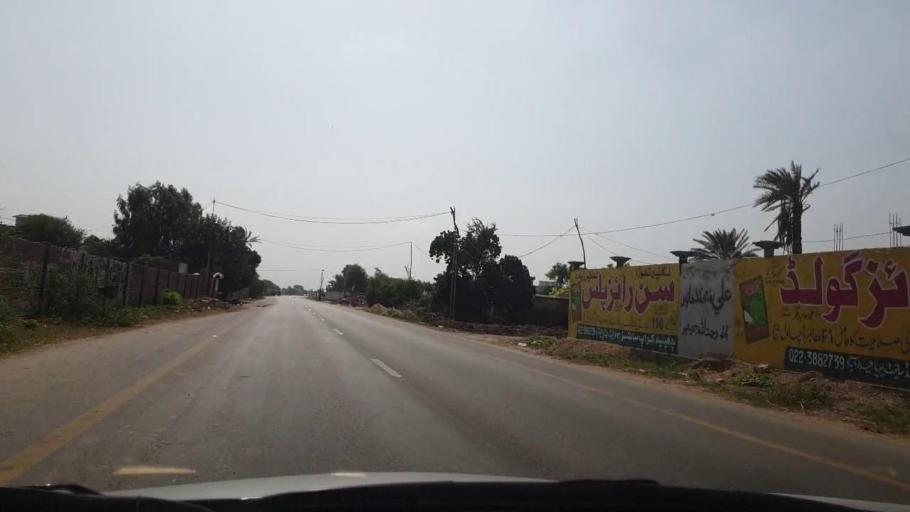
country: PK
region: Sindh
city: Matli
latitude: 25.0744
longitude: 68.6186
